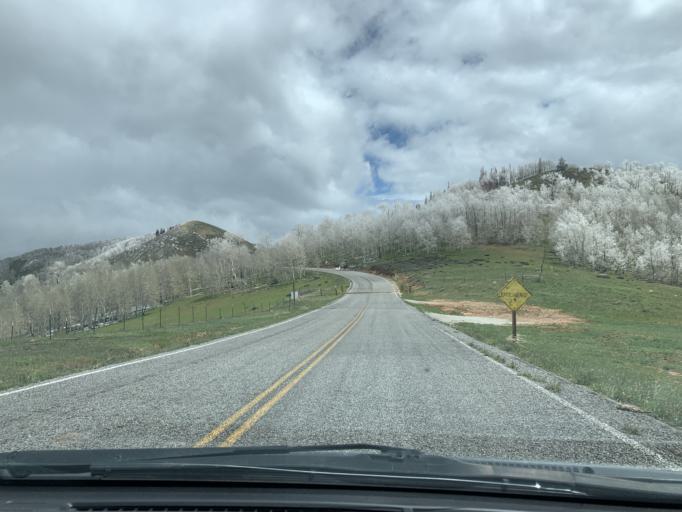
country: US
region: Utah
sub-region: Utah County
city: Santaquin
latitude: 39.8595
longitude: -111.6959
